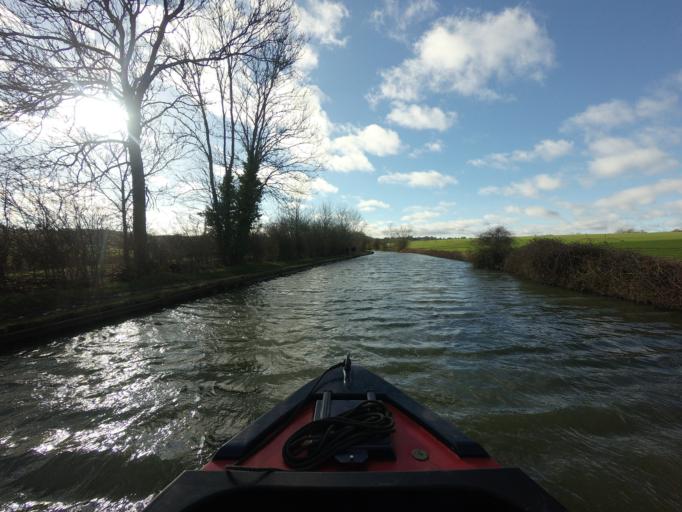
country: GB
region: England
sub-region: Northamptonshire
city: Bugbrooke
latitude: 52.2204
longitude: -1.0428
